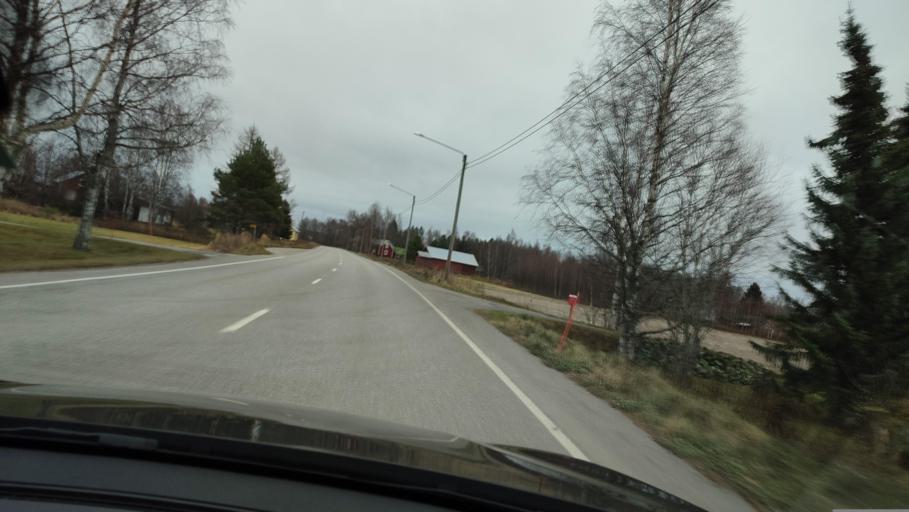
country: FI
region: Southern Ostrobothnia
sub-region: Suupohja
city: Karijoki
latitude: 62.2318
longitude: 21.6234
